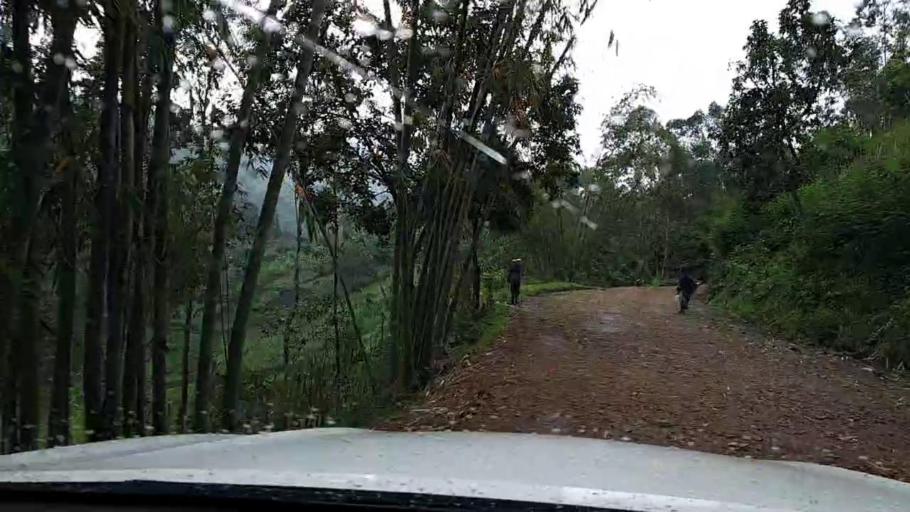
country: RW
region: Western Province
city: Cyangugu
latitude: -2.5366
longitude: 29.0419
